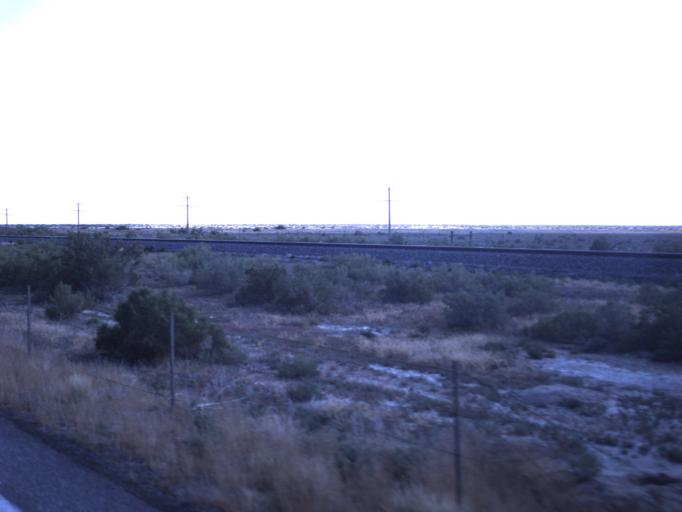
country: US
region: Utah
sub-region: Millard County
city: Delta
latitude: 38.9477
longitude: -112.8066
